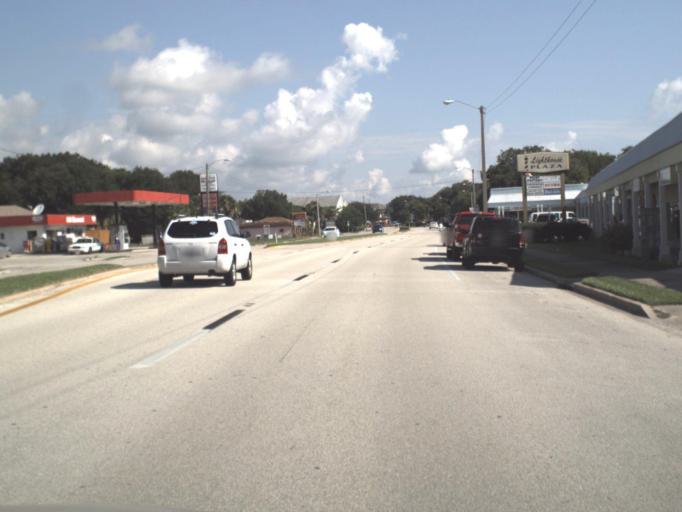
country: US
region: Florida
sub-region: Saint Johns County
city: Saint Augustine
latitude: 29.8856
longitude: -81.2907
